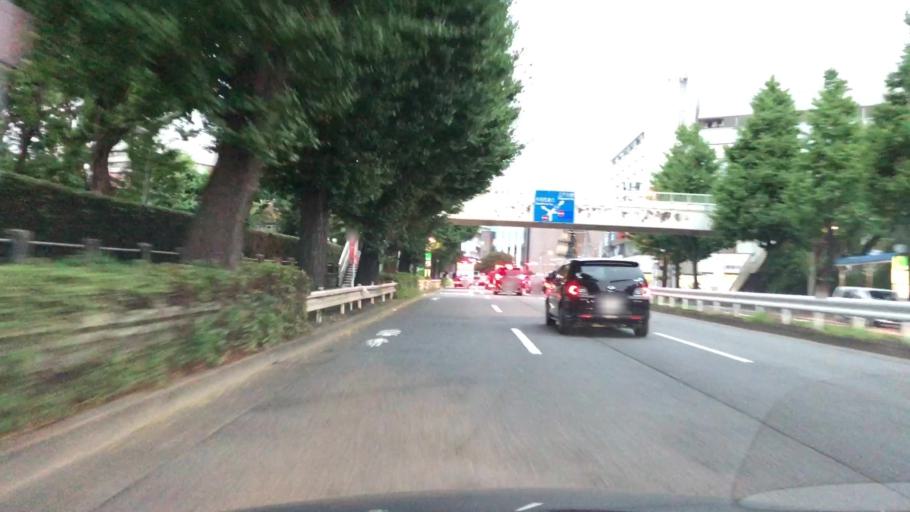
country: JP
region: Tokyo
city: Tokyo
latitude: 35.6790
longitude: 139.7199
